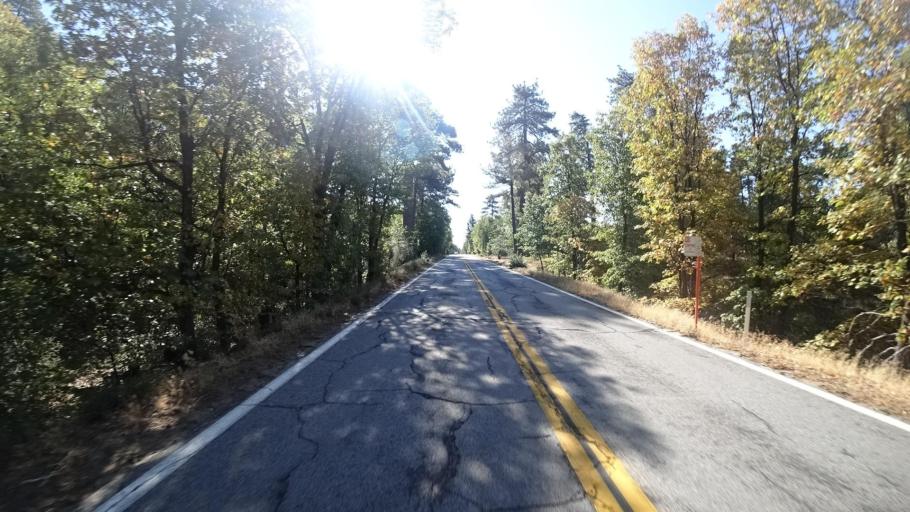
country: US
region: California
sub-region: San Diego County
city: Pine Valley
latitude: 32.8789
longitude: -116.4227
